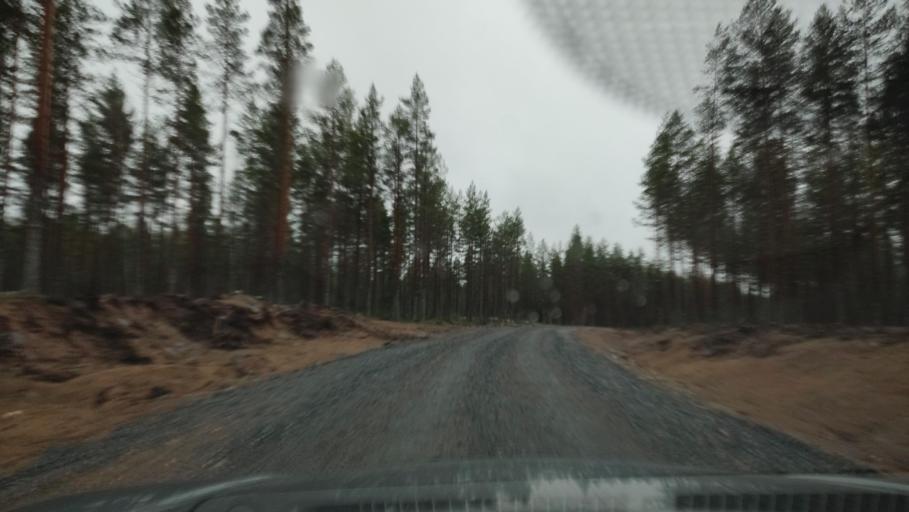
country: FI
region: Southern Ostrobothnia
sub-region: Suupohja
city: Karijoki
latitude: 62.1575
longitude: 21.6124
